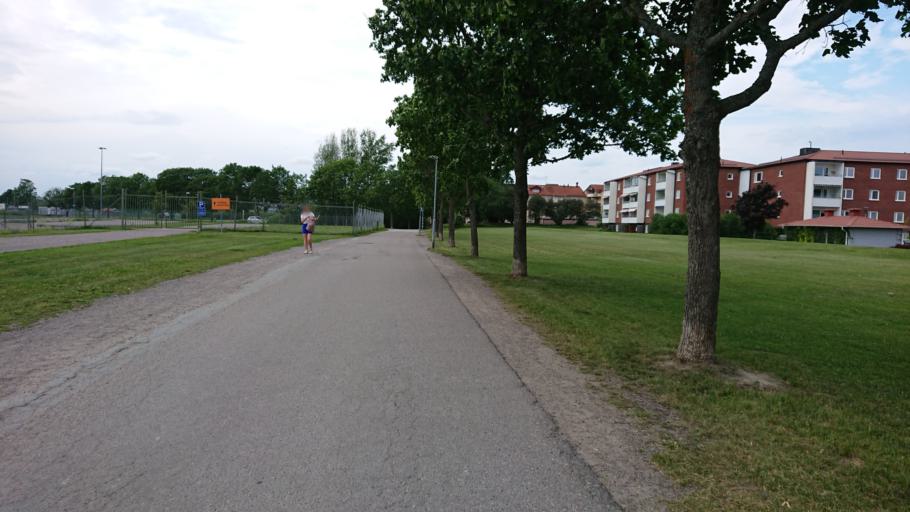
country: SE
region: Uppsala
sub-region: Uppsala Kommun
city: Uppsala
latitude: 59.8721
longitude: 17.6212
